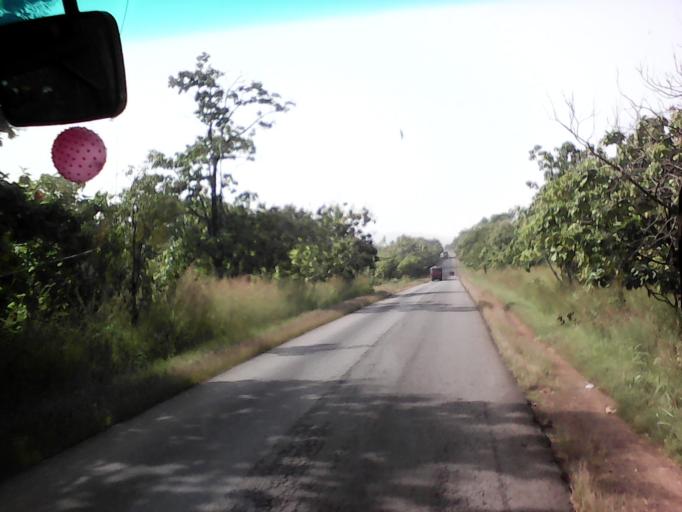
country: TG
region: Centrale
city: Sokode
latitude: 9.1162
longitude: 1.1455
